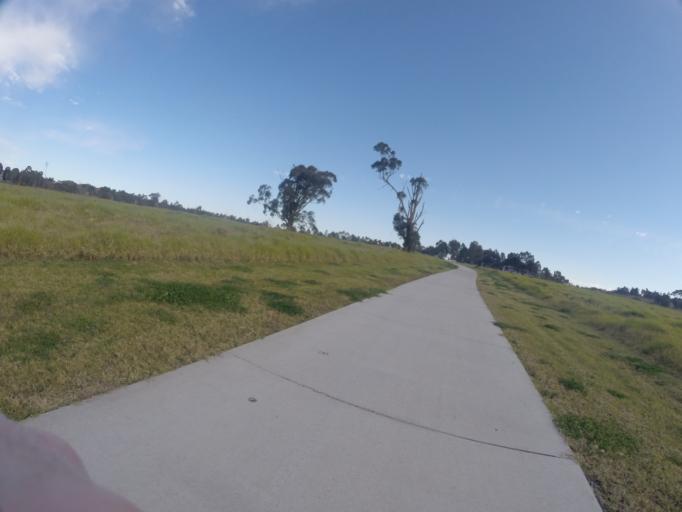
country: AU
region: New South Wales
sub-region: Fairfield
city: Horsley Park
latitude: -33.8600
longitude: 150.8697
